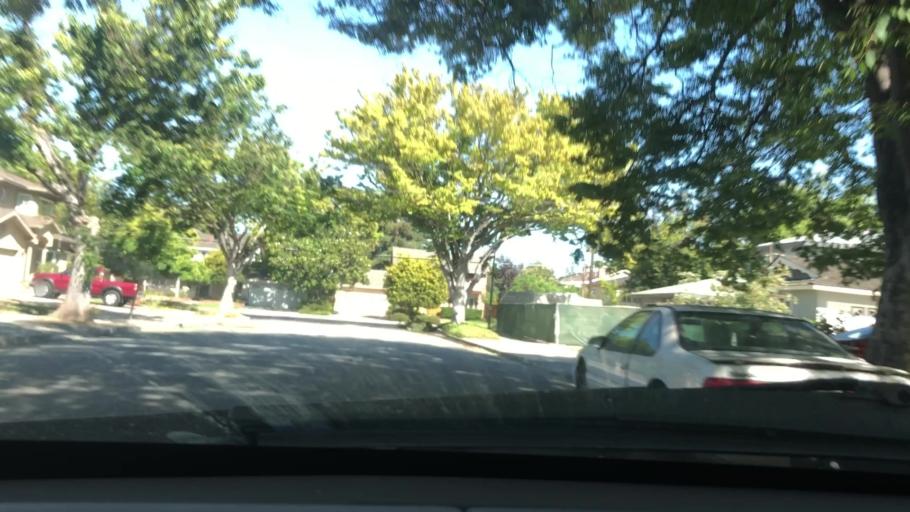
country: US
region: California
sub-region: Santa Clara County
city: Campbell
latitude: 37.3023
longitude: -121.9915
